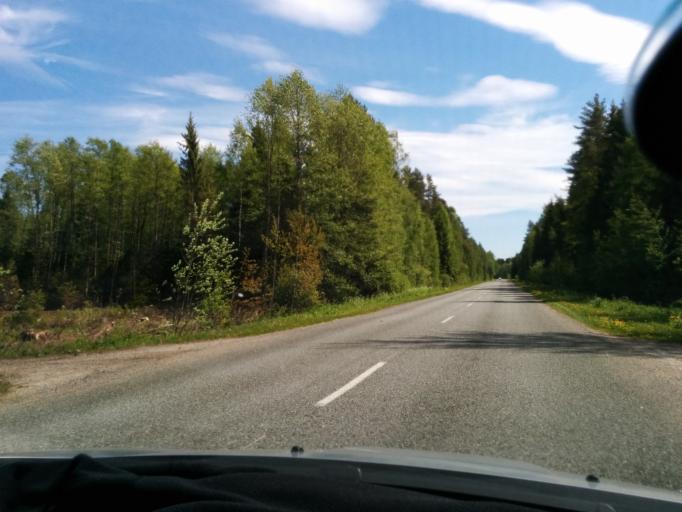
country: EE
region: Harju
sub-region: Loksa linn
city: Loksa
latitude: 59.5649
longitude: 25.9489
